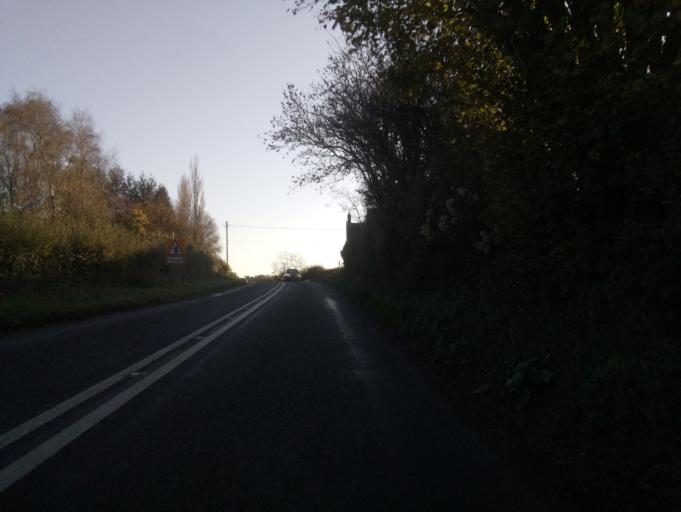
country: GB
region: England
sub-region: Somerset
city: Wincanton
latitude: 51.0308
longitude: -2.4383
